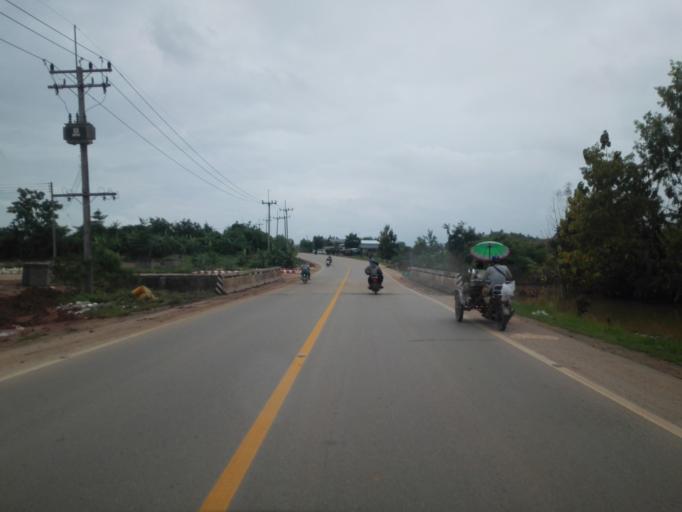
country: TH
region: Tak
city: Mae Sot
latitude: 16.6873
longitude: 98.4690
